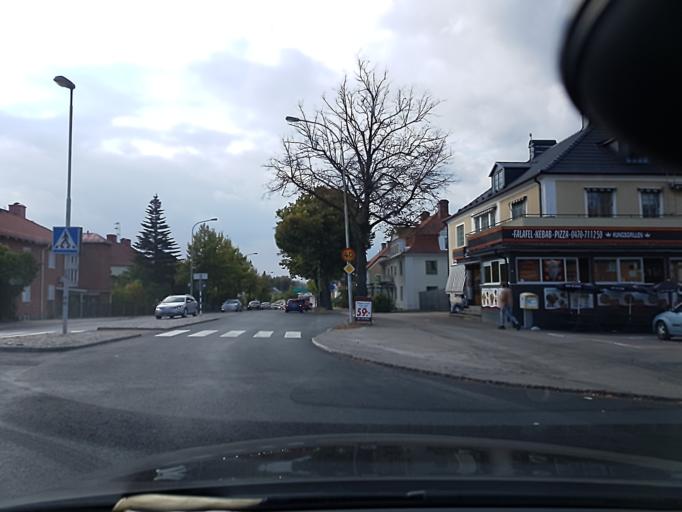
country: SE
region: Kronoberg
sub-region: Vaxjo Kommun
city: Vaexjoe
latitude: 56.8788
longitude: 14.7892
